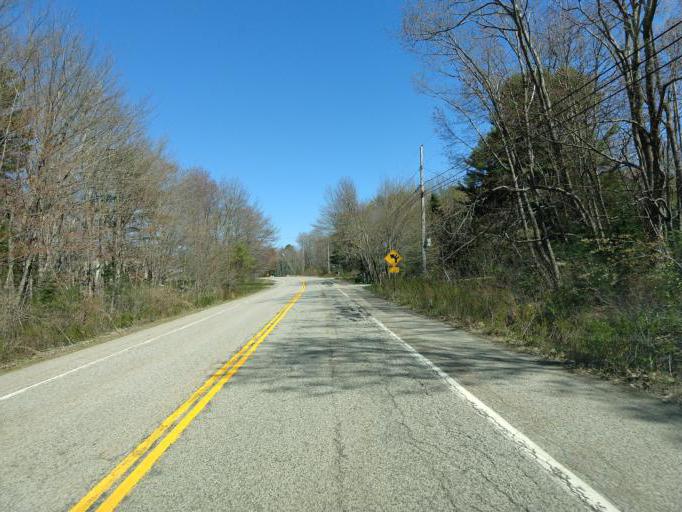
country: US
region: Maine
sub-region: York County
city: Biddeford
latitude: 43.4249
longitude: -70.3929
